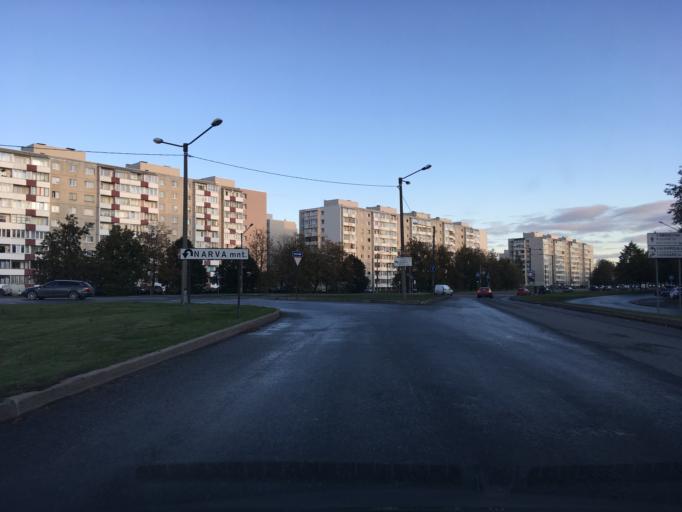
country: EE
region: Harju
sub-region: Tallinna linn
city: Kose
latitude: 59.4384
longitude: 24.8259
